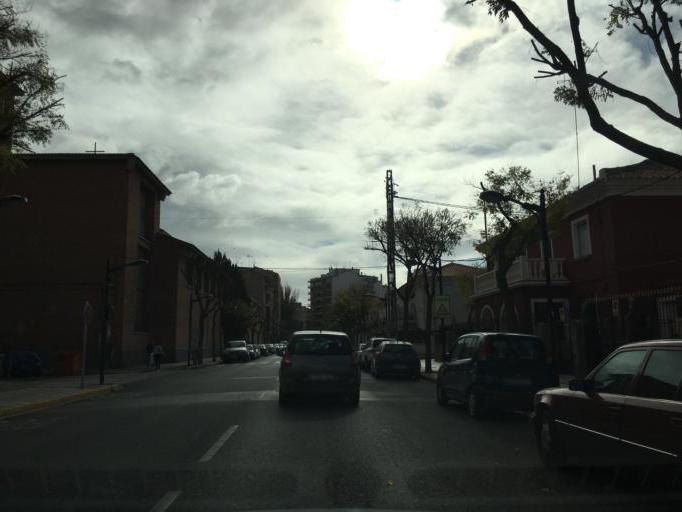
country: ES
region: Castille-La Mancha
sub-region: Provincia de Albacete
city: Albacete
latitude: 38.9931
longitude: -1.8669
